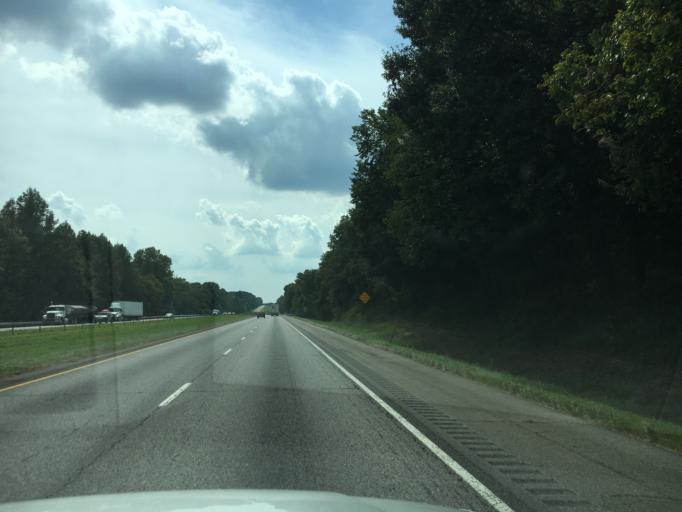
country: US
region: Georgia
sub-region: Franklin County
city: Carnesville
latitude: 34.3719
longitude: -83.2683
